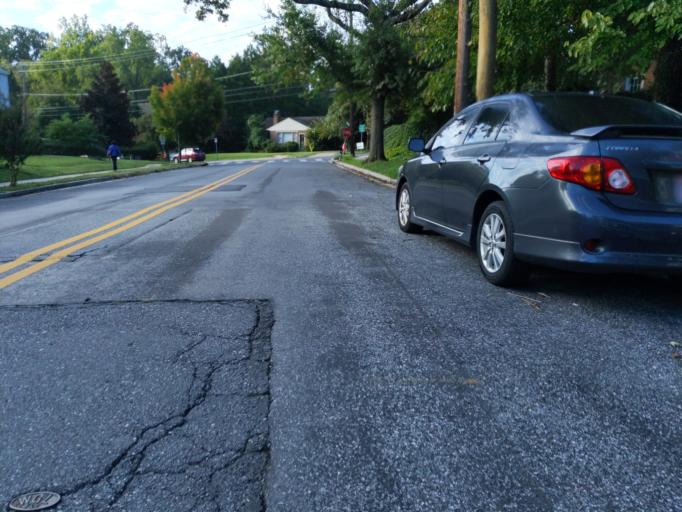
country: US
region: Maryland
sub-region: Montgomery County
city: Forest Glen
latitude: 39.0205
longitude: -77.0507
